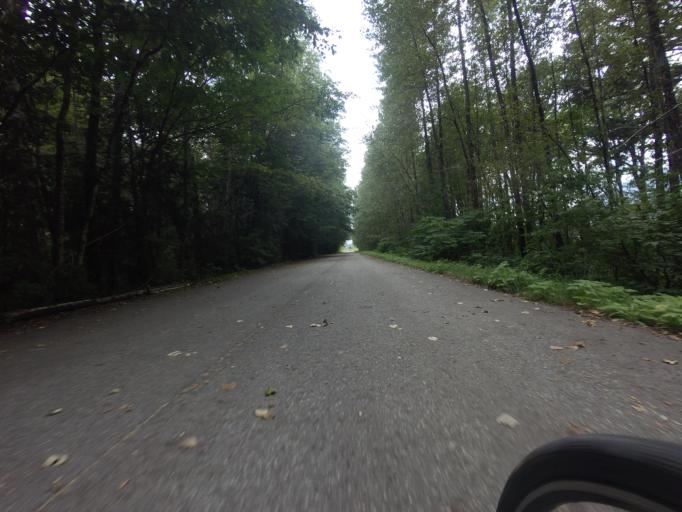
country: CA
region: British Columbia
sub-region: Greater Vancouver Regional District
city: Lions Bay
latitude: 49.7276
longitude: -123.1481
